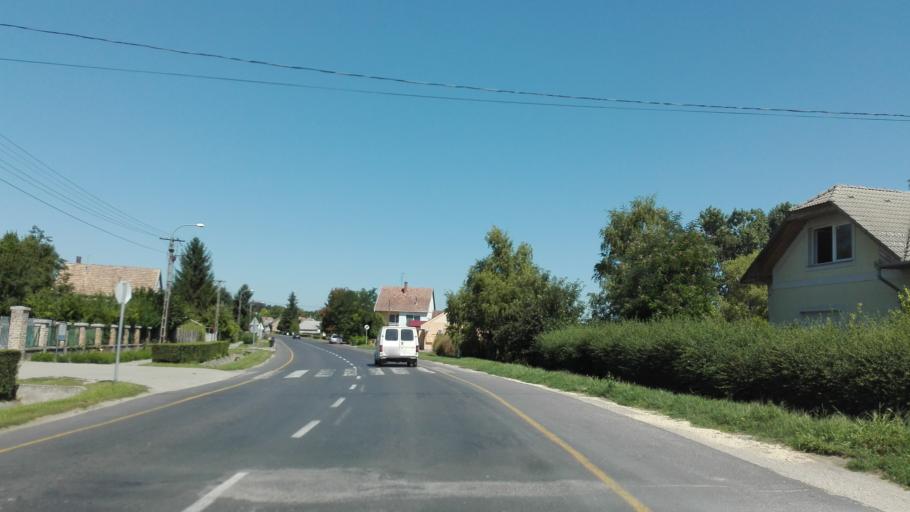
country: HU
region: Fejer
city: Mezoszilas
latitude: 46.8146
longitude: 18.4813
